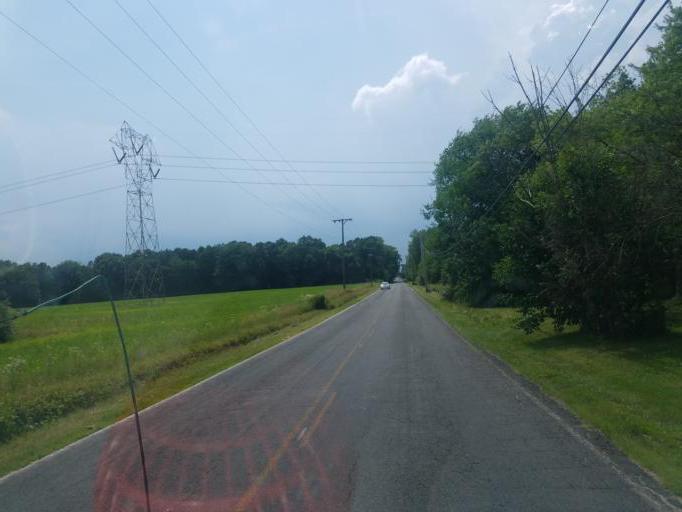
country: US
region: Ohio
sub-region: Portage County
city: Ravenna
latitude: 41.1107
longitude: -81.2238
